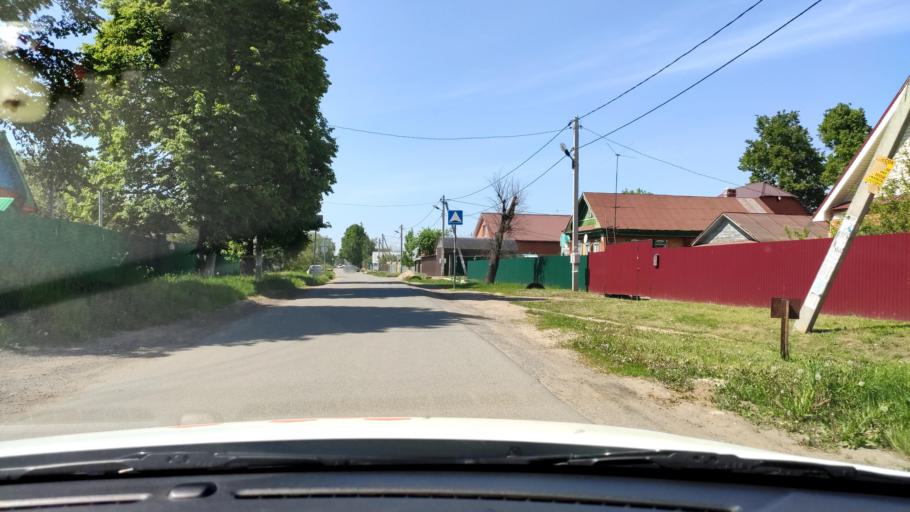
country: RU
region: Tatarstan
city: Osinovo
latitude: 55.8464
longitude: 48.9008
